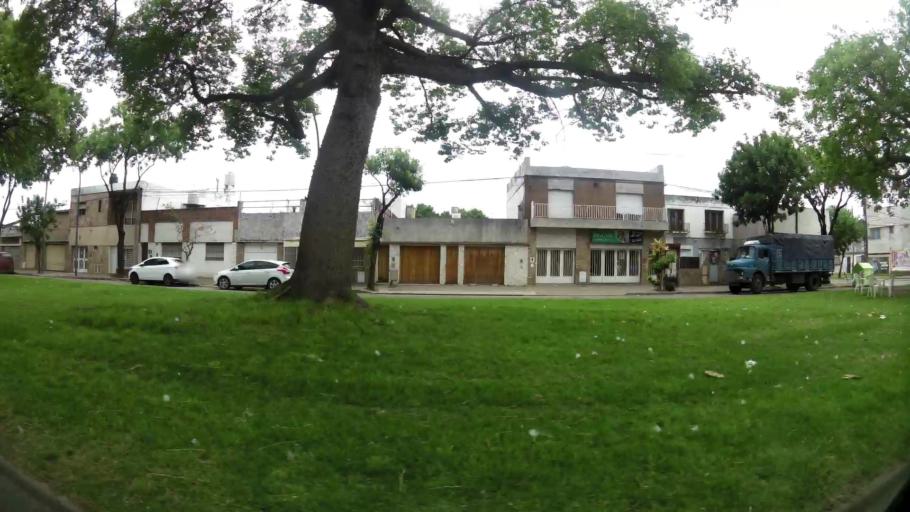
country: AR
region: Santa Fe
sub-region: Departamento de Rosario
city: Rosario
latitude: -32.9771
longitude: -60.6569
